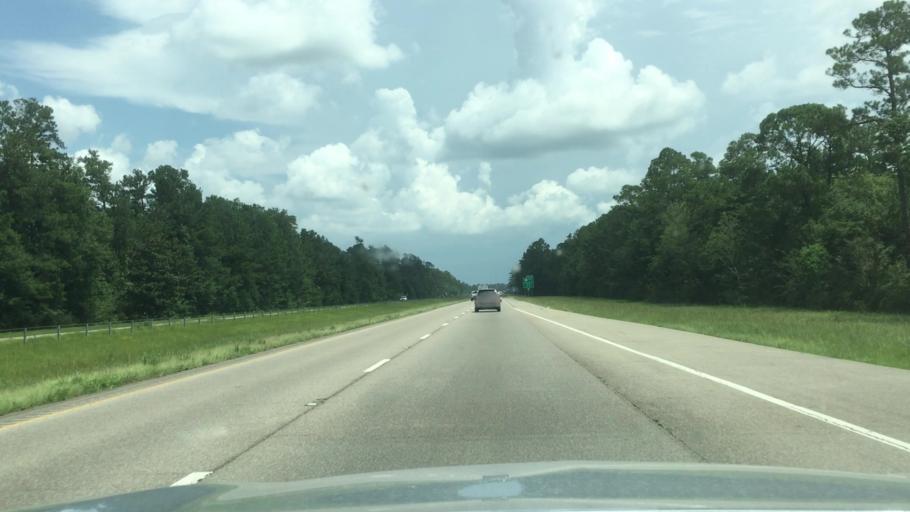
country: US
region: Mississippi
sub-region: Pearl River County
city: Picayune
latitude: 30.5023
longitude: -89.6685
